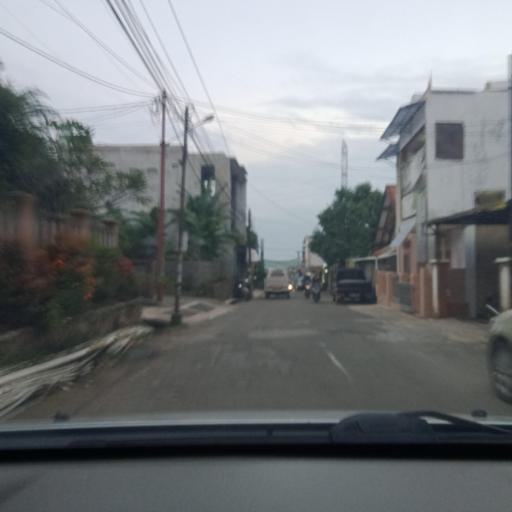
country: ID
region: West Java
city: Cimahi
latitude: -6.8489
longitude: 107.5819
